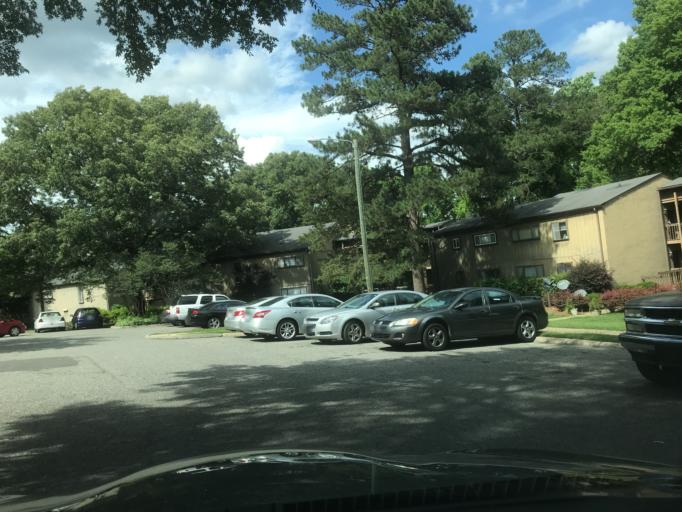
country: US
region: North Carolina
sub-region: Wake County
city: West Raleigh
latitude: 35.8526
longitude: -78.6276
